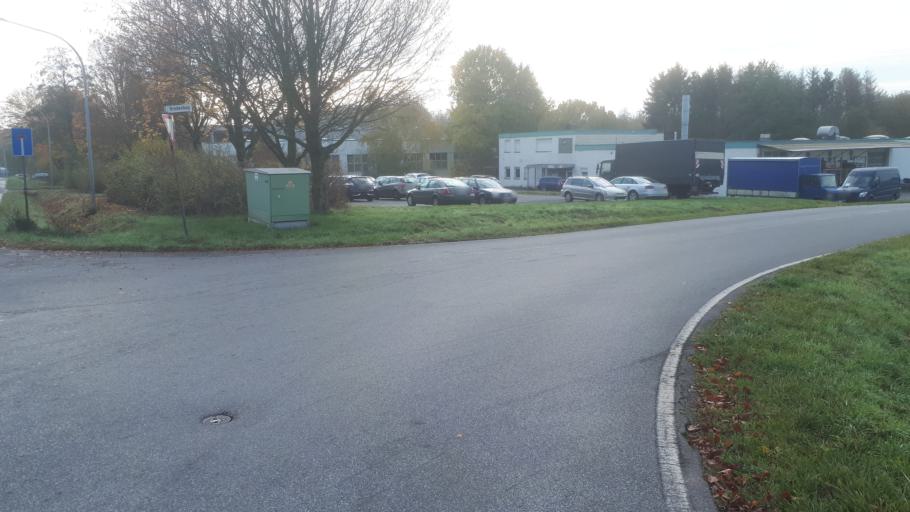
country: DE
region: North Rhine-Westphalia
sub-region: Regierungsbezirk Detmold
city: Huellhorst
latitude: 52.2691
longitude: 8.7078
